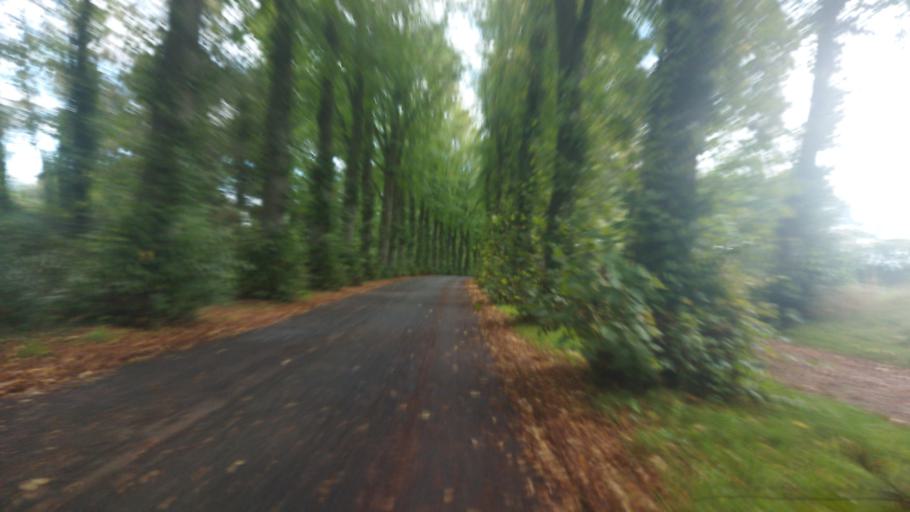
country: DE
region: North Rhine-Westphalia
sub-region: Regierungsbezirk Munster
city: Haltern
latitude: 51.7513
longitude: 7.2050
